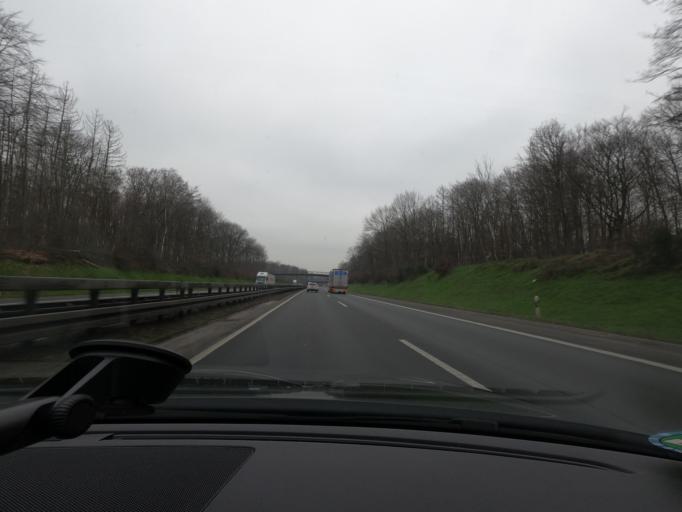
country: DE
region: North Rhine-Westphalia
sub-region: Regierungsbezirk Dusseldorf
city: Viersen
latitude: 51.2195
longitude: 6.3715
